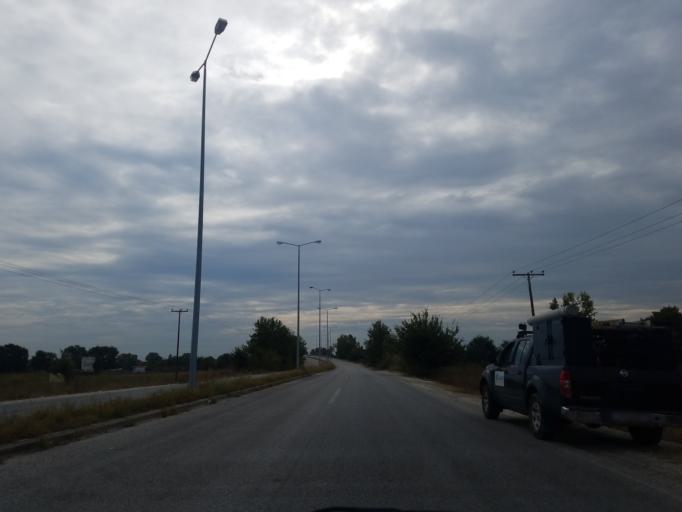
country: GR
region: Thessaly
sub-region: Trikala
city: Pyrgetos
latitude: 39.5233
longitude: 21.7518
